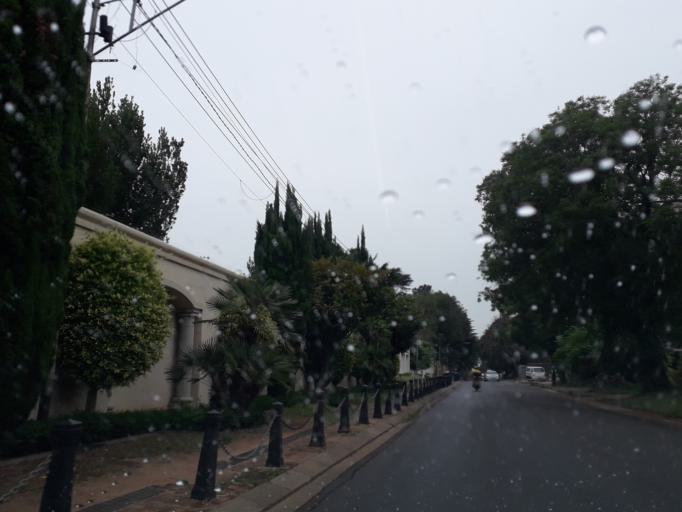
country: ZA
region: Gauteng
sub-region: City of Johannesburg Metropolitan Municipality
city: Johannesburg
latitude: -26.1251
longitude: 28.0464
